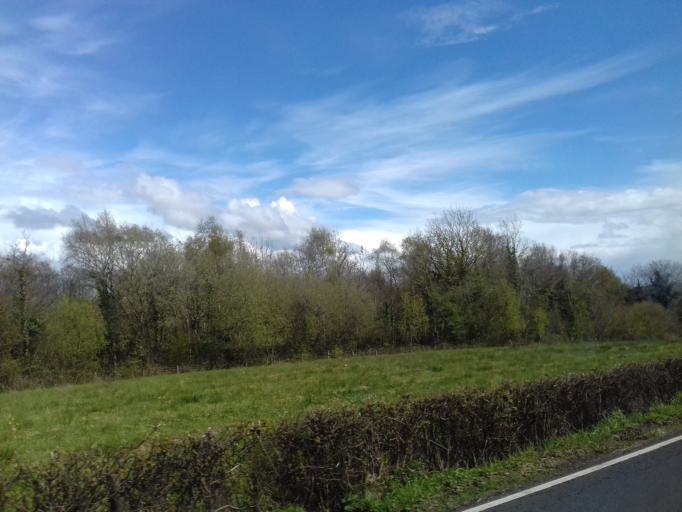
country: GB
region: Northern Ireland
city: Irvinestown
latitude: 54.4459
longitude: -7.7940
